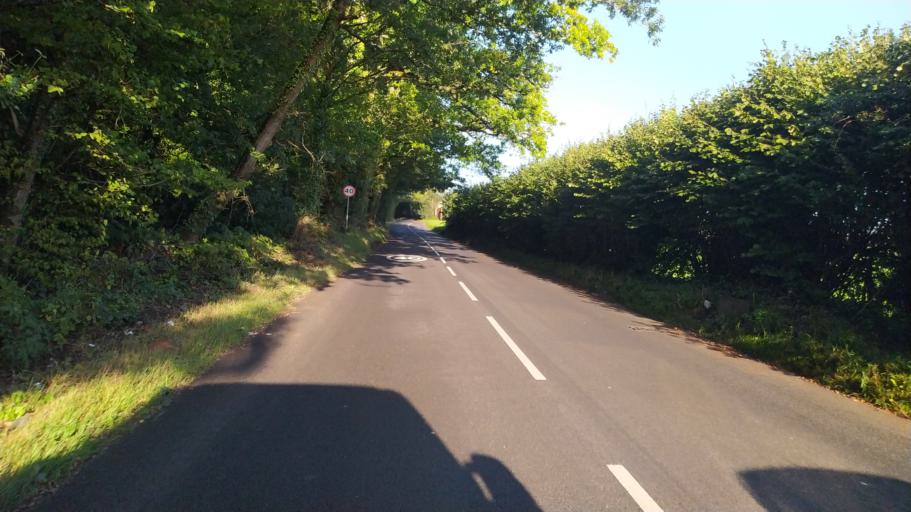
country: GB
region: England
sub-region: Dorset
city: Three Legged Cross
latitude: 50.8602
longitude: -1.9274
